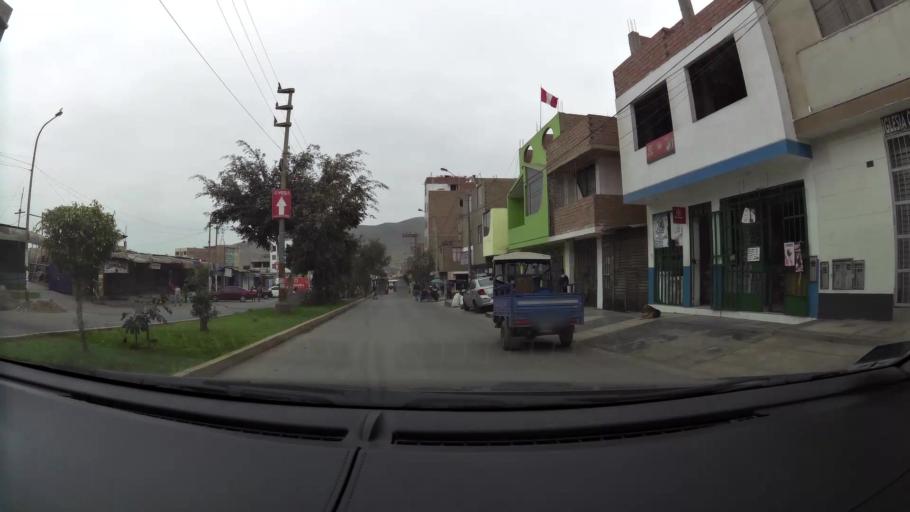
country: PE
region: Lima
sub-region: Lima
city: Independencia
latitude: -11.9457
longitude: -77.0865
